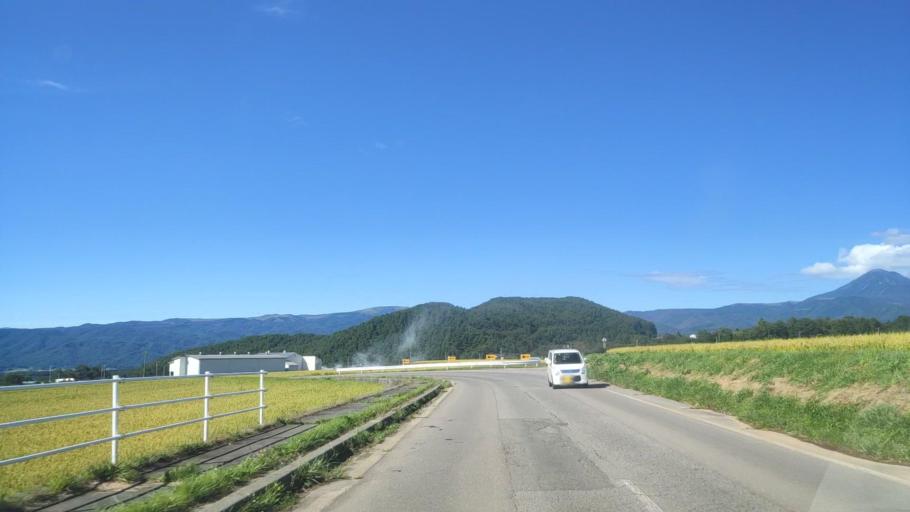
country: JP
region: Nagano
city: Chino
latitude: 35.9876
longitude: 138.2175
